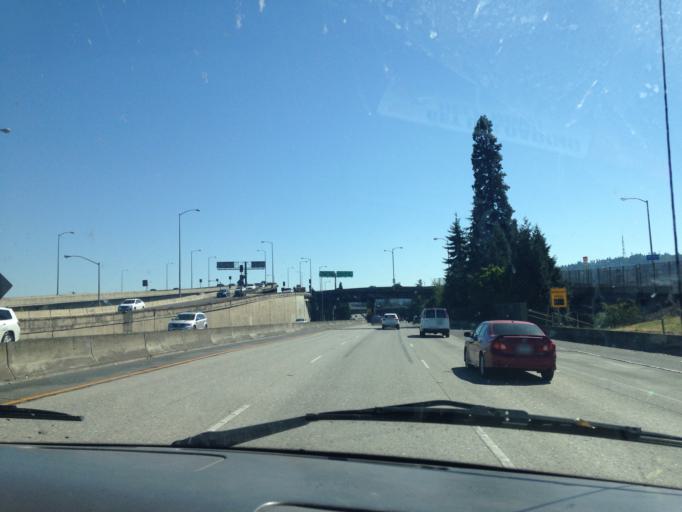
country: US
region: Oregon
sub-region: Multnomah County
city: Portland
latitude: 45.5208
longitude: -122.6659
